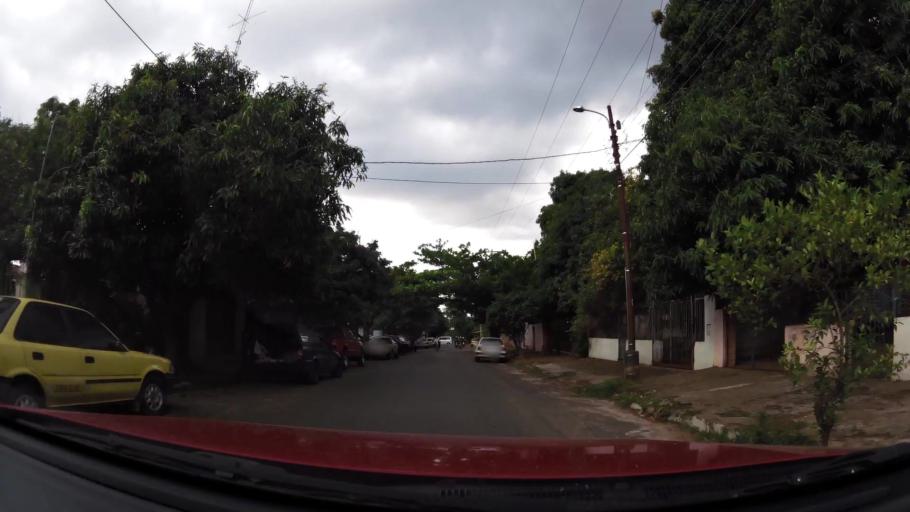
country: PY
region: Central
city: Fernando de la Mora
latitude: -25.3386
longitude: -57.5601
